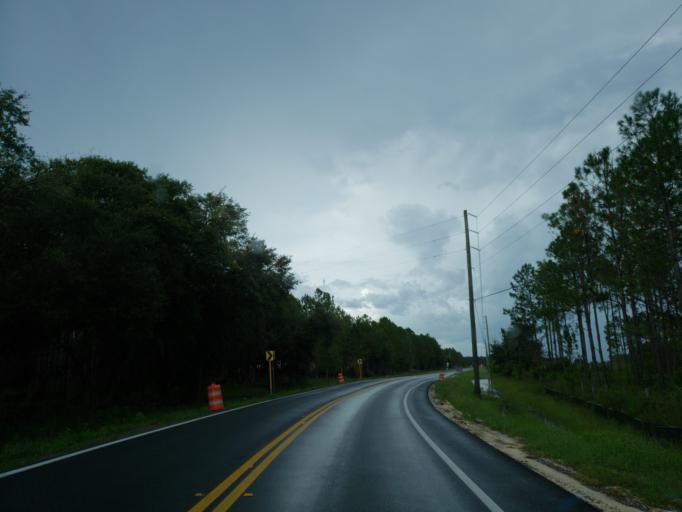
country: US
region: Florida
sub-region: Pasco County
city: Land O' Lakes
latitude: 28.3160
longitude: -82.4204
